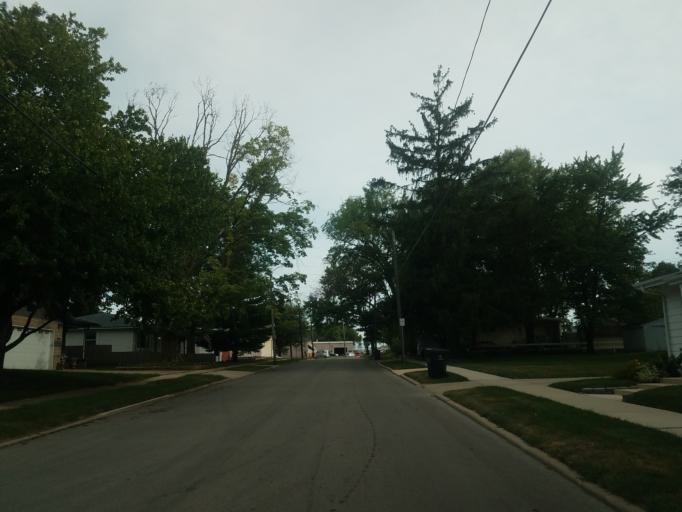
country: US
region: Illinois
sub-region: McLean County
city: Bloomington
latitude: 40.4677
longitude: -88.9855
